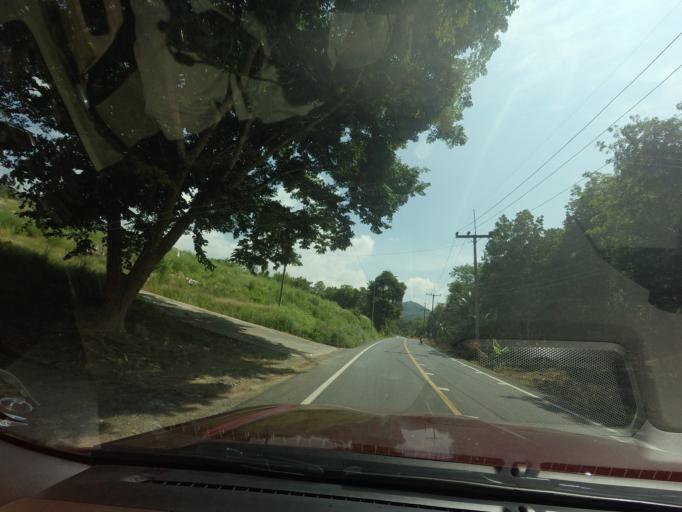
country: TH
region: Yala
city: Betong
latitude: 5.8092
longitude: 101.0735
